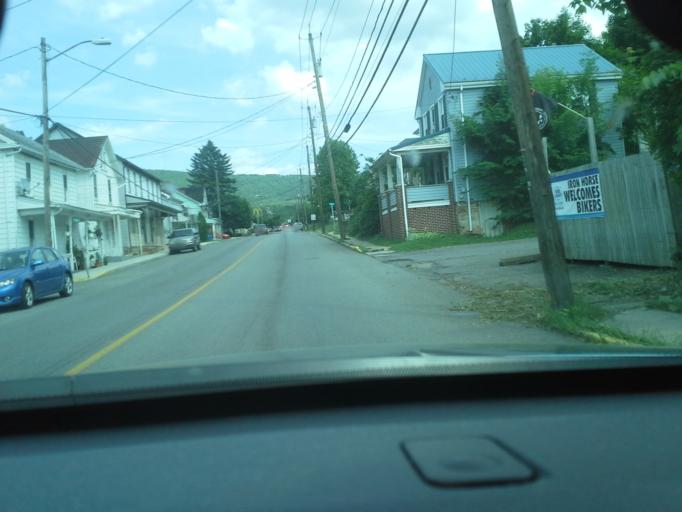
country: US
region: Pennsylvania
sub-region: Fulton County
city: McConnellsburg
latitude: 39.9310
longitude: -77.9946
